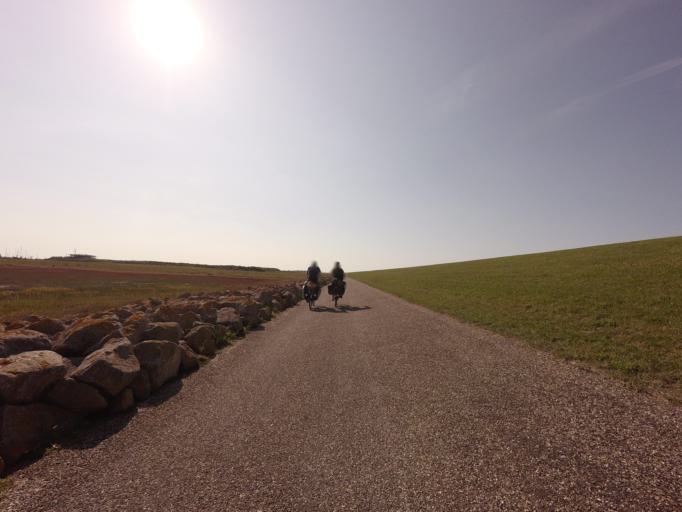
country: NL
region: Friesland
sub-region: Gemeente Schiermonnikoog
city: Schiermonnikoog
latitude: 53.4726
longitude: 6.1702
